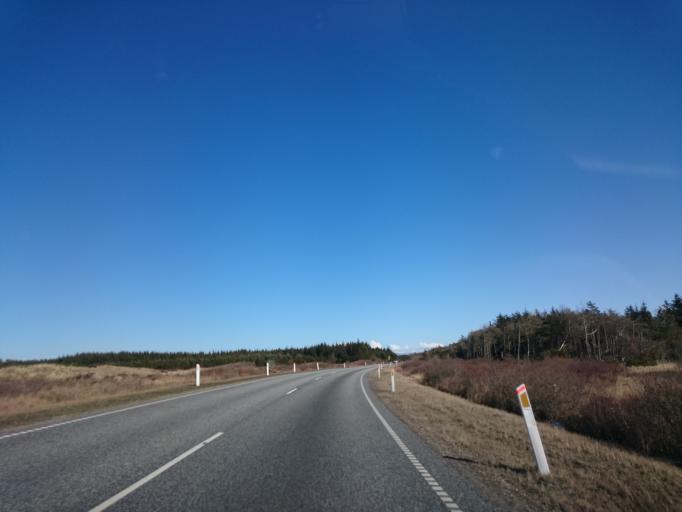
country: DK
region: North Denmark
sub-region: Frederikshavn Kommune
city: Skagen
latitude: 57.6972
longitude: 10.4787
